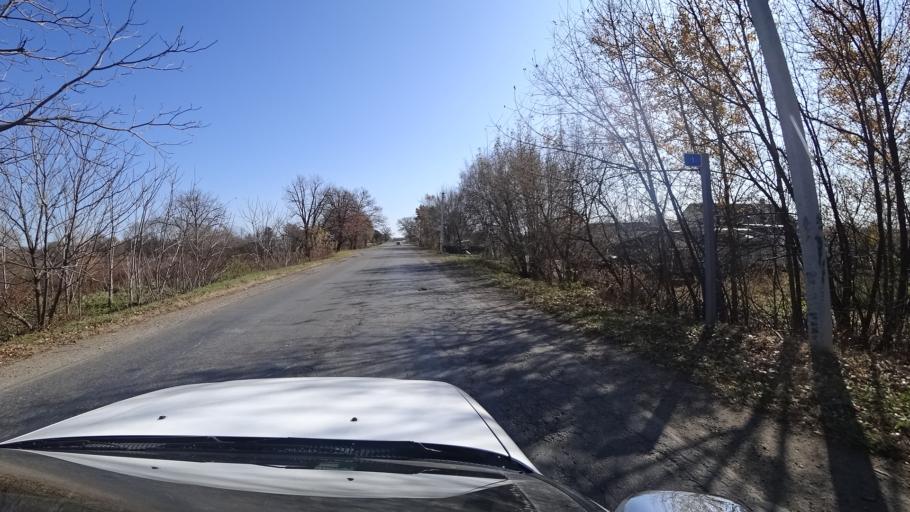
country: RU
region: Primorskiy
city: Dal'nerechensk
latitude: 45.9162
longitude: 133.7844
